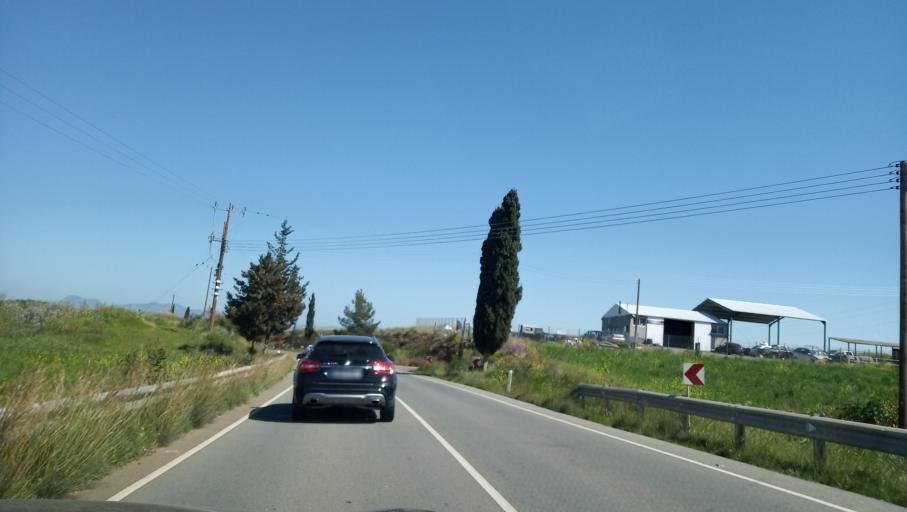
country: CY
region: Lefkosia
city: Astromeritis
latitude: 35.1172
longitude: 33.0069
